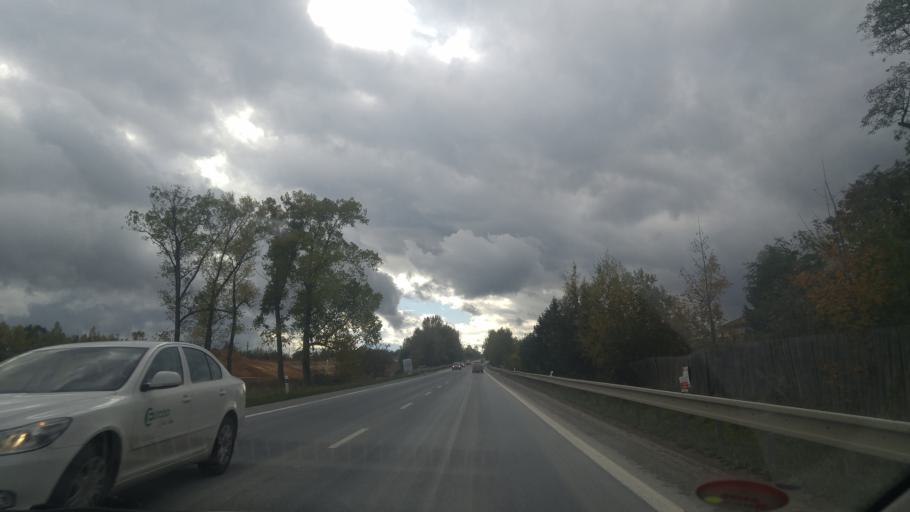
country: CZ
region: Jihocesky
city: Sevetin
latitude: 49.1300
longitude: 14.6079
